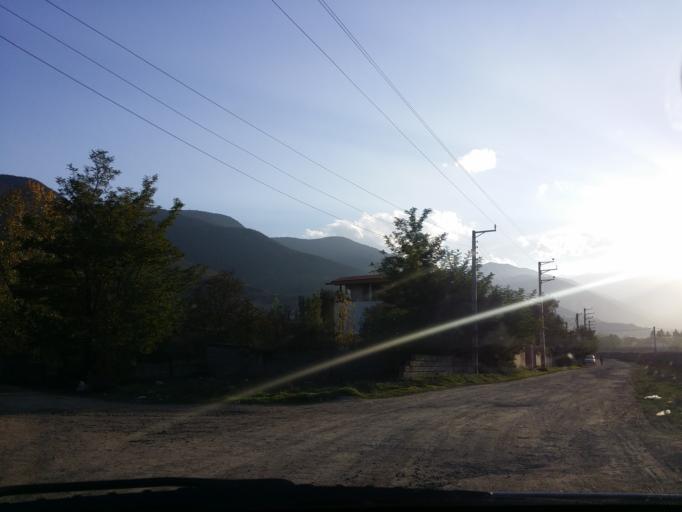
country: IR
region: Mazandaran
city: `Abbasabad
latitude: 36.5116
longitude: 51.1899
